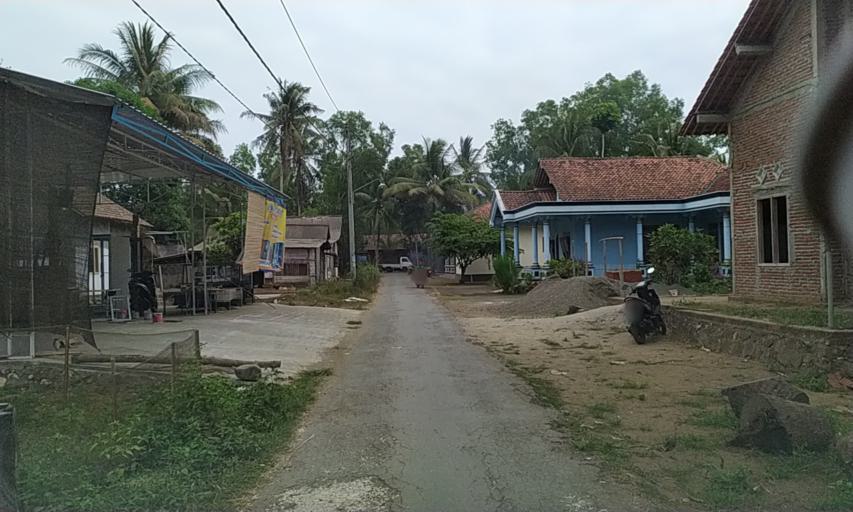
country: ID
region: Central Java
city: Kroya
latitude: -7.6981
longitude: 109.3125
